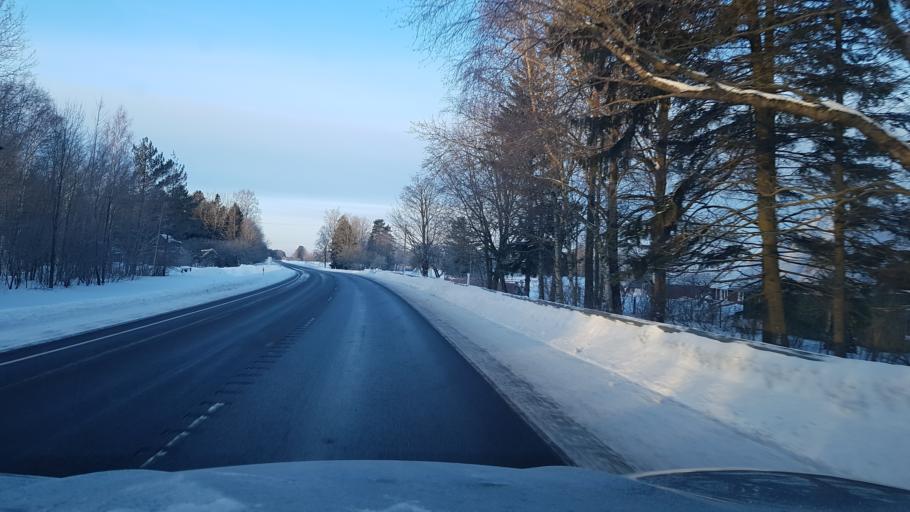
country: EE
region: Ida-Virumaa
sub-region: Toila vald
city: Voka
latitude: 59.3939
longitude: 27.6335
